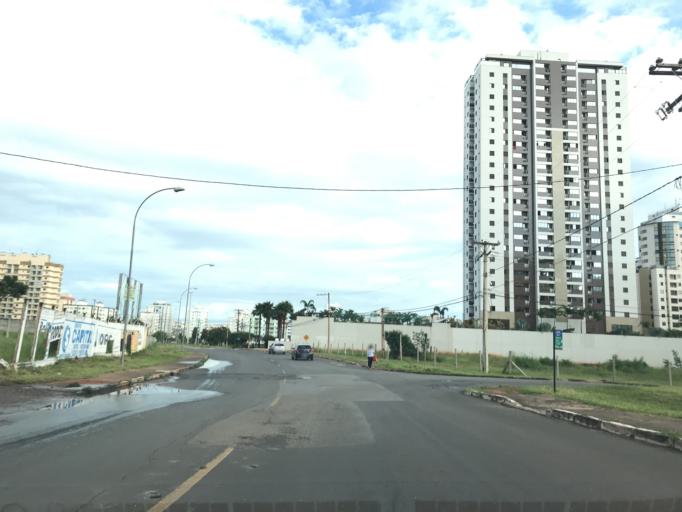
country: BR
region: Federal District
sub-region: Brasilia
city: Brasilia
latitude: -15.8328
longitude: -48.0114
